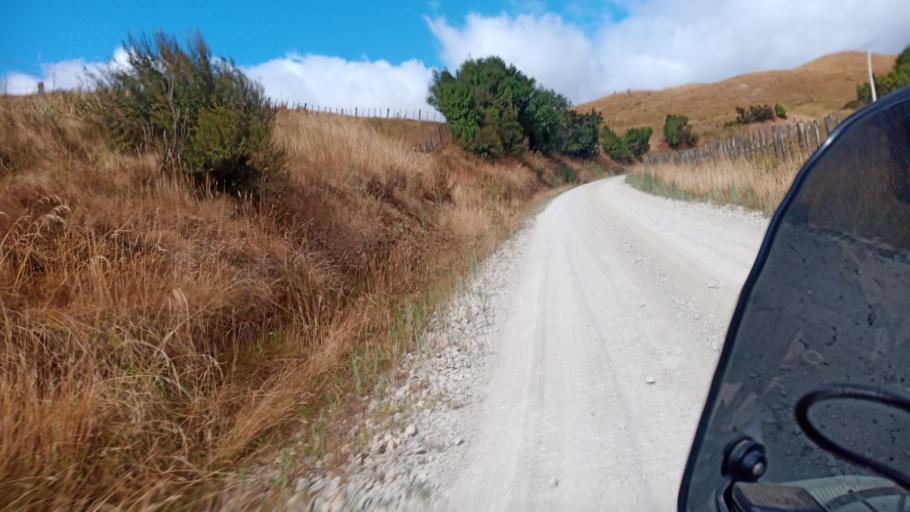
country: NZ
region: Hawke's Bay
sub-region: Wairoa District
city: Wairoa
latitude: -38.6031
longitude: 177.4799
